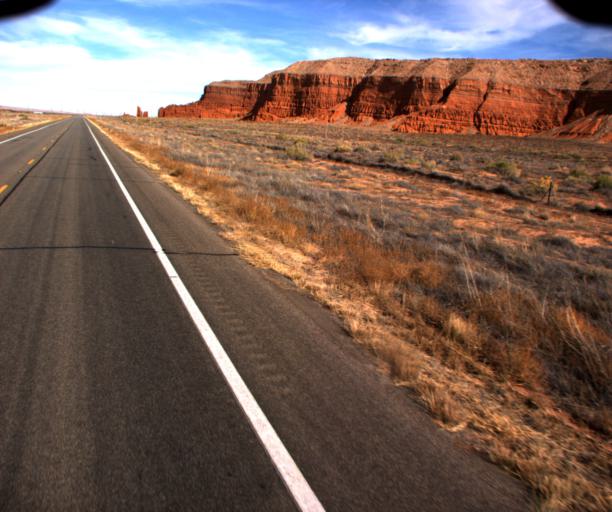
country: US
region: Arizona
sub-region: Navajo County
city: Kayenta
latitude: 36.7702
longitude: -110.0261
